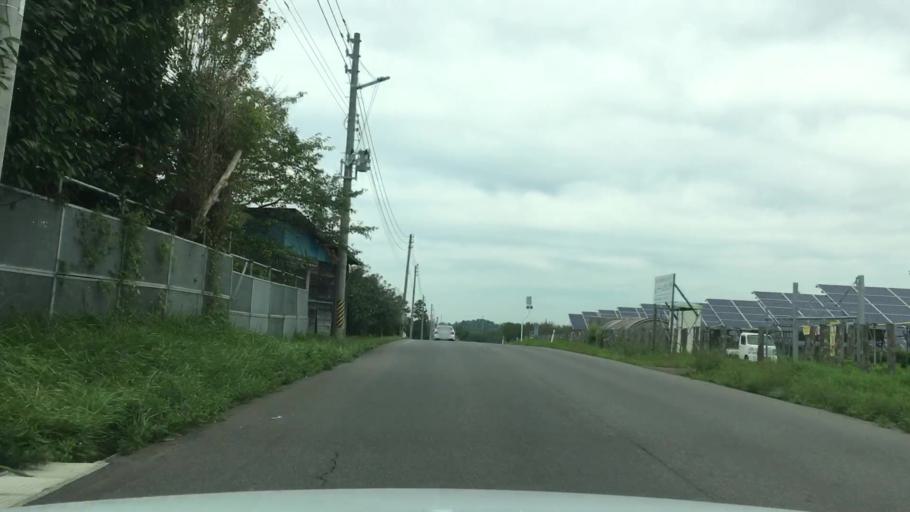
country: JP
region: Aomori
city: Hirosaki
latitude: 40.6536
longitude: 140.4213
